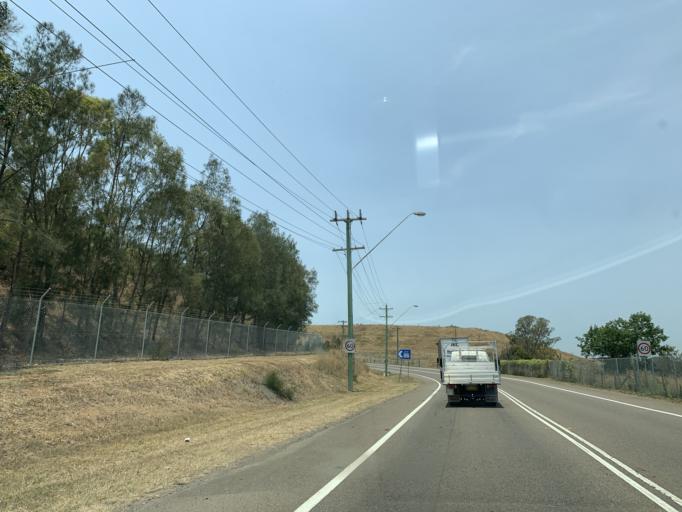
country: AU
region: New South Wales
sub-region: Fairfield
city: Horsley Park
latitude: -33.8073
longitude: 150.8641
